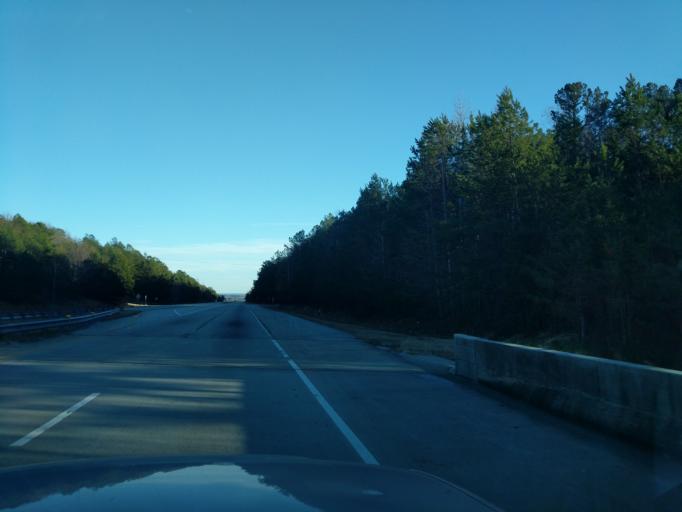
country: US
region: Georgia
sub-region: Stephens County
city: Toccoa
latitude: 34.5624
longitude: -83.3936
